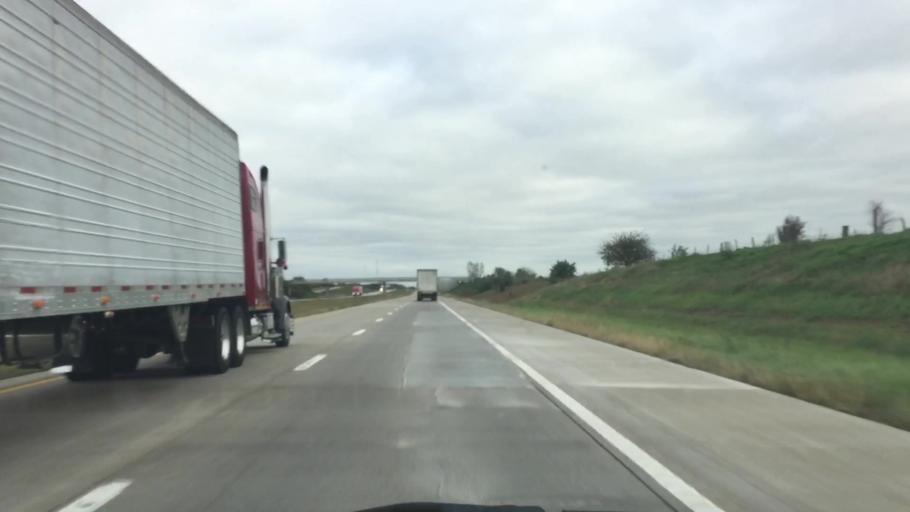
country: US
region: Missouri
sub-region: Clinton County
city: Lathrop
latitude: 39.5833
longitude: -94.2583
